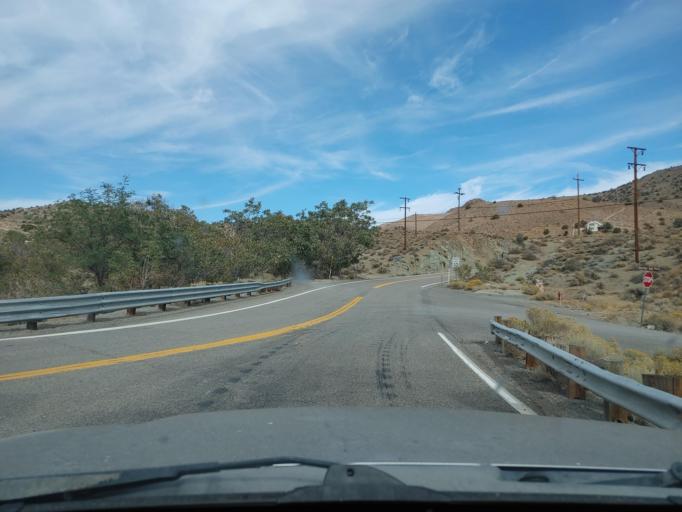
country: US
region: Nevada
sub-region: Lyon County
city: Dayton
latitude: 39.2578
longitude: -119.6358
